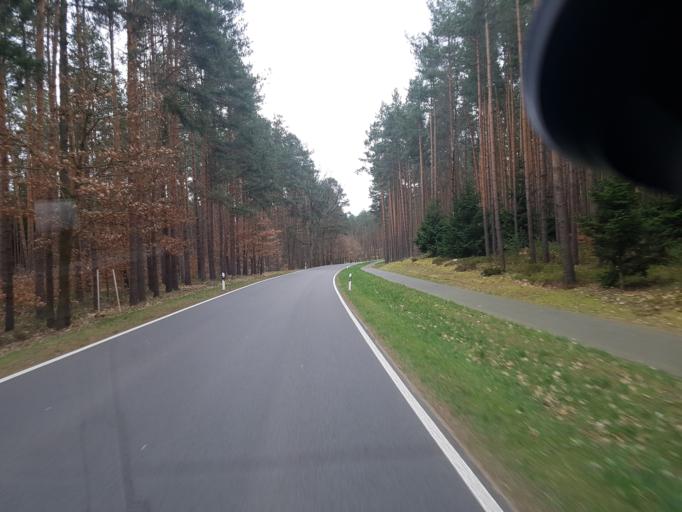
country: DE
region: Brandenburg
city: Gross Lindow
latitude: 52.1630
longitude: 14.5034
